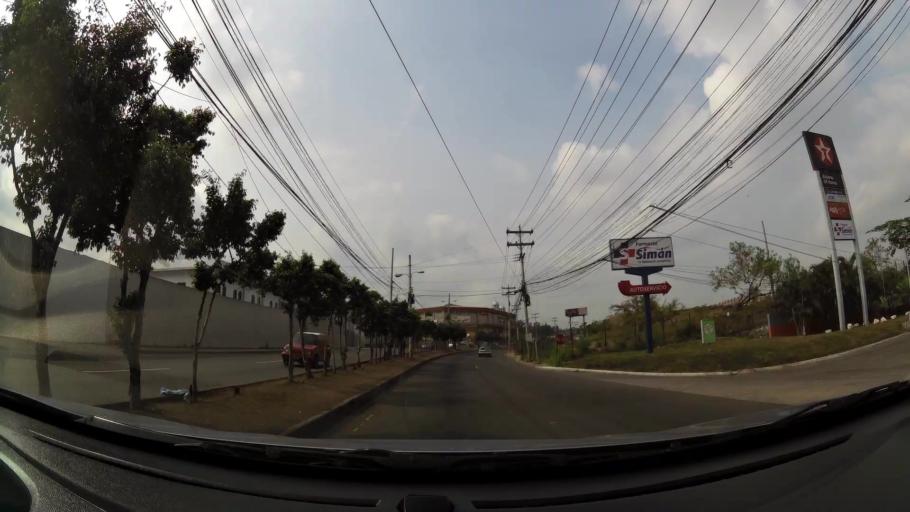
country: HN
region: Francisco Morazan
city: Santa Lucia
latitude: 14.0859
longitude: -87.1577
